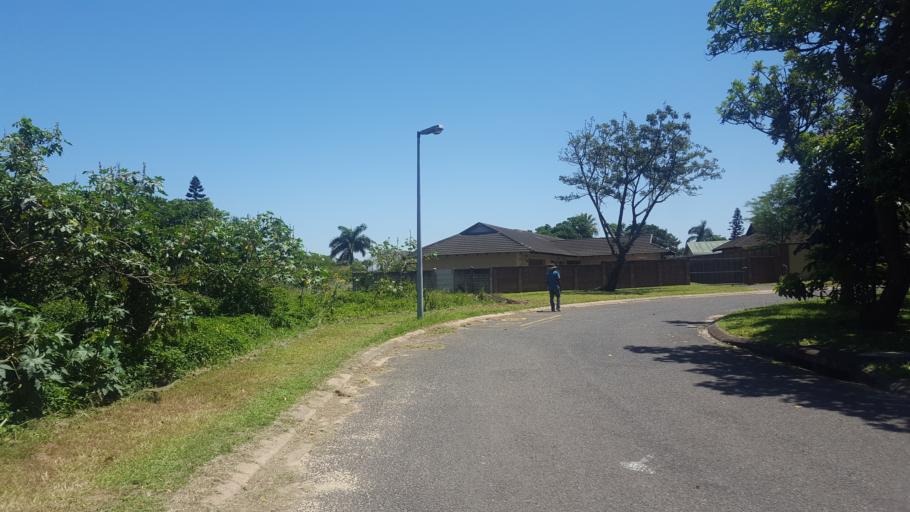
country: ZA
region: KwaZulu-Natal
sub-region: uThungulu District Municipality
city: Richards Bay
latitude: -28.7642
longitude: 32.0690
